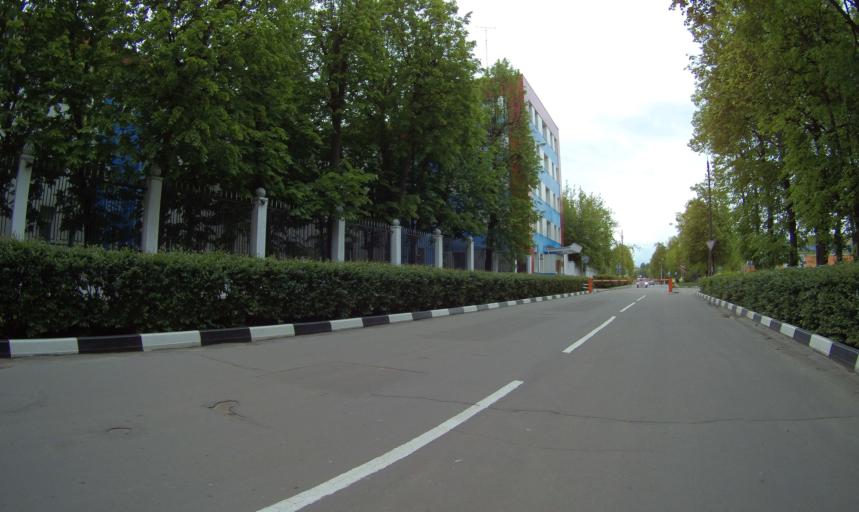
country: RU
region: Moskovskaya
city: Kolomna
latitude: 55.0702
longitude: 38.8038
